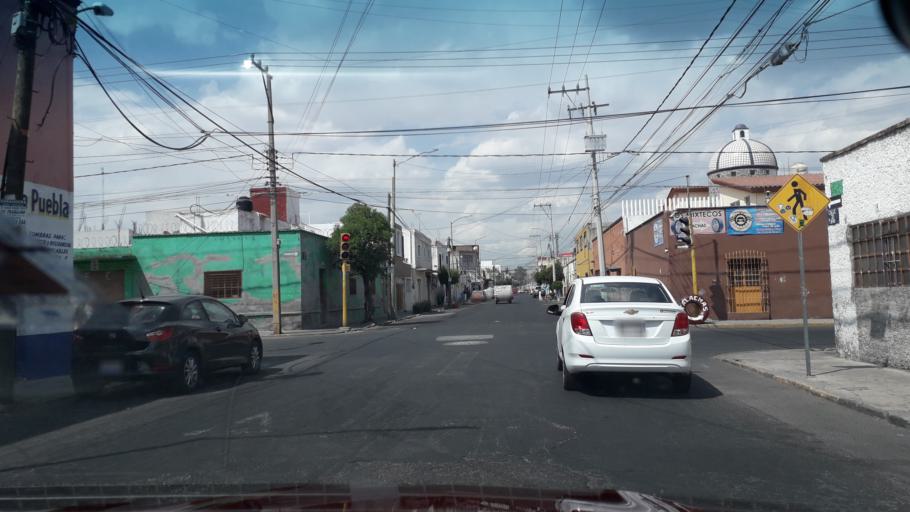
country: MX
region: Puebla
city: Puebla
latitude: 19.0443
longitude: -98.2180
